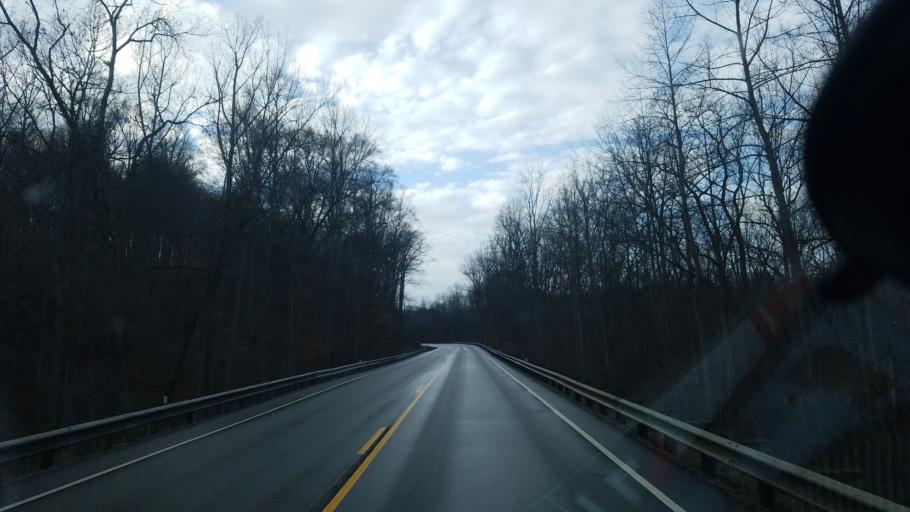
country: US
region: Ohio
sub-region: Knox County
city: Oak Hill
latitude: 40.3407
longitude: -82.0987
